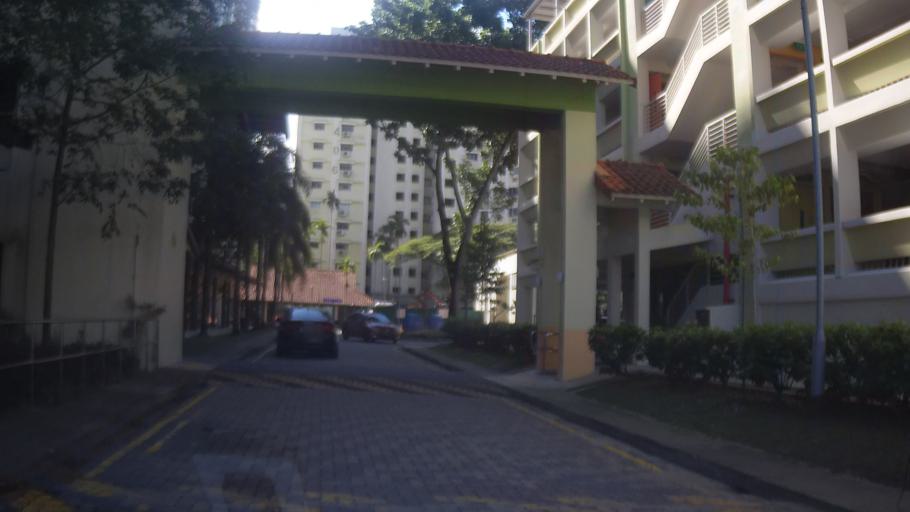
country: MY
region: Johor
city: Johor Bahru
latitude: 1.4300
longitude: 103.7721
